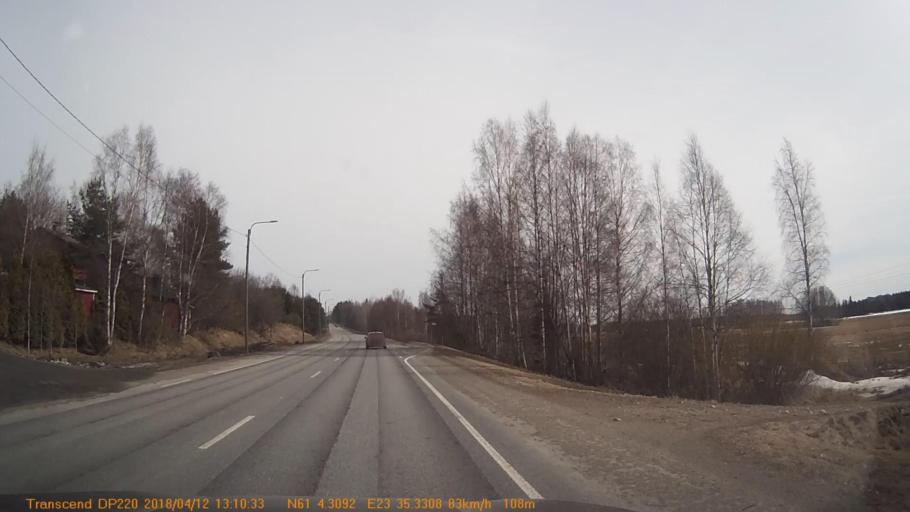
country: FI
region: Pirkanmaa
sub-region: Etelae-Pirkanmaa
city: Urjala
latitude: 61.0717
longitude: 23.5904
